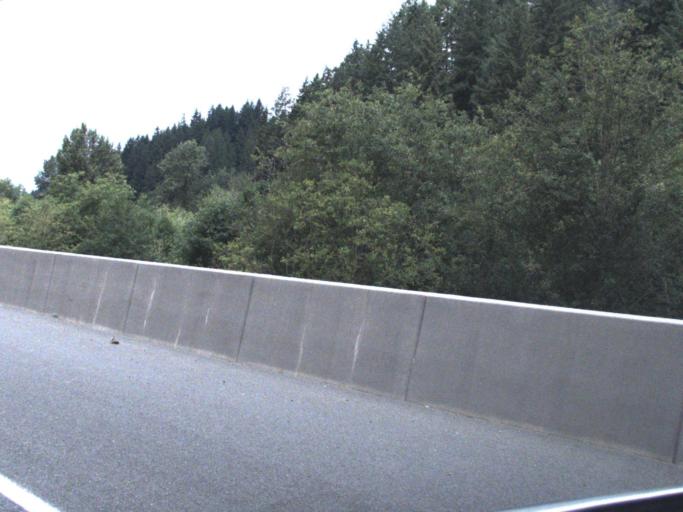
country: US
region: Washington
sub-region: Snohomish County
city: Cathcart
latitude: 47.8314
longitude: -122.0431
